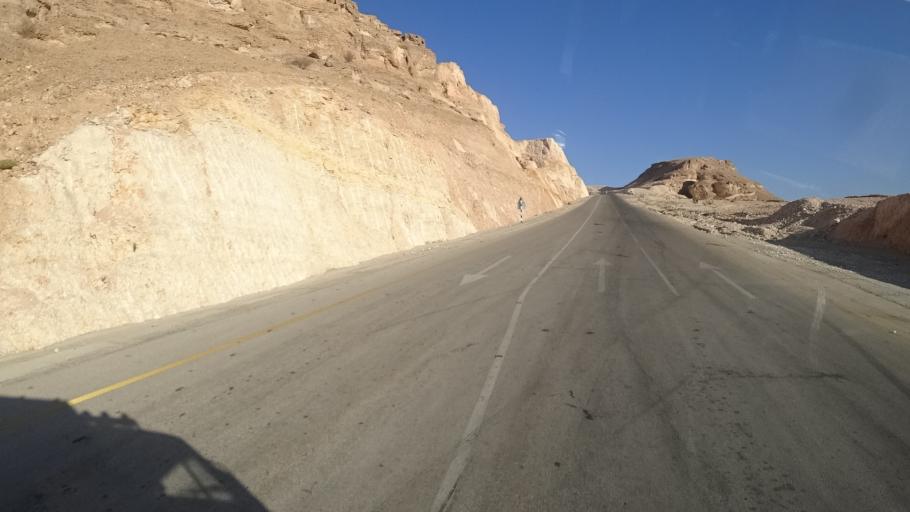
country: YE
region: Al Mahrah
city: Hawf
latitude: 17.0941
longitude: 53.0592
